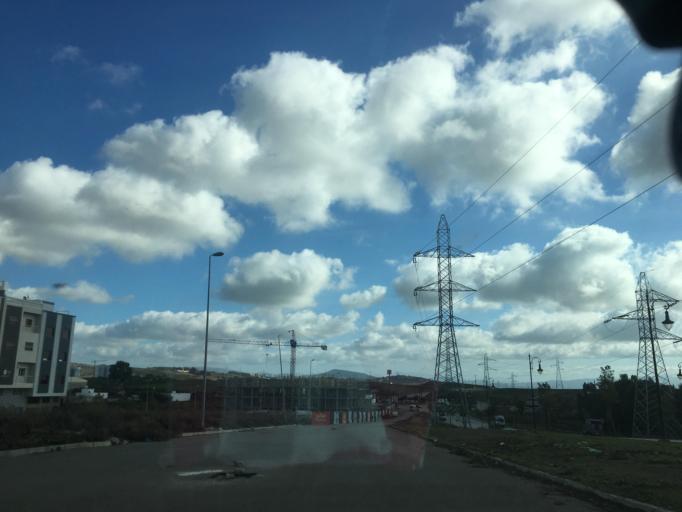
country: MA
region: Tanger-Tetouan
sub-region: Tanger-Assilah
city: Tangier
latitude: 35.7084
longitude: -5.8167
